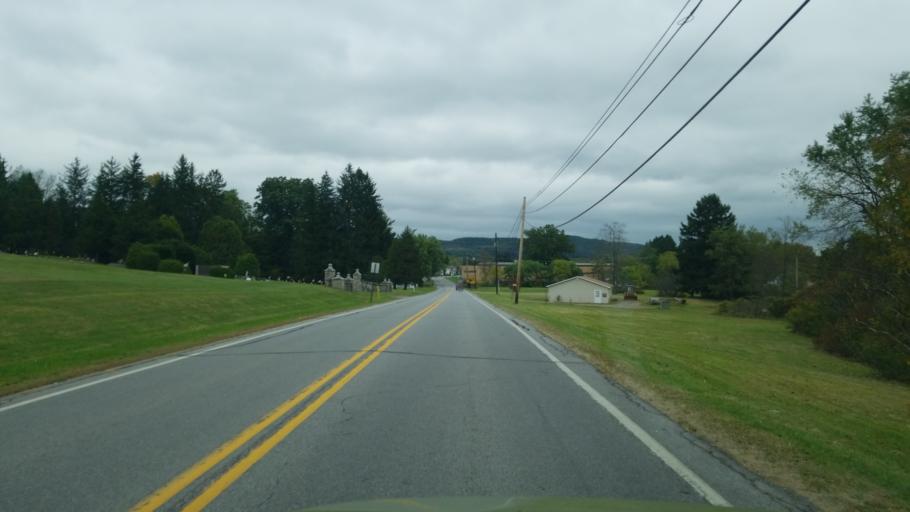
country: US
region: Pennsylvania
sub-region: Clearfield County
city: Hyde
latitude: 40.9945
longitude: -78.4672
